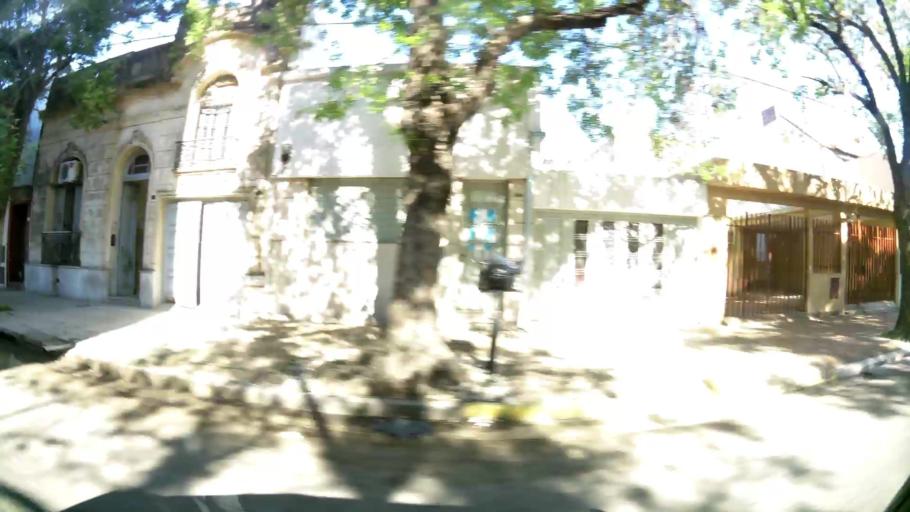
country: AR
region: Santa Fe
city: Santa Fe de la Vera Cruz
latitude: -31.6418
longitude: -60.7162
